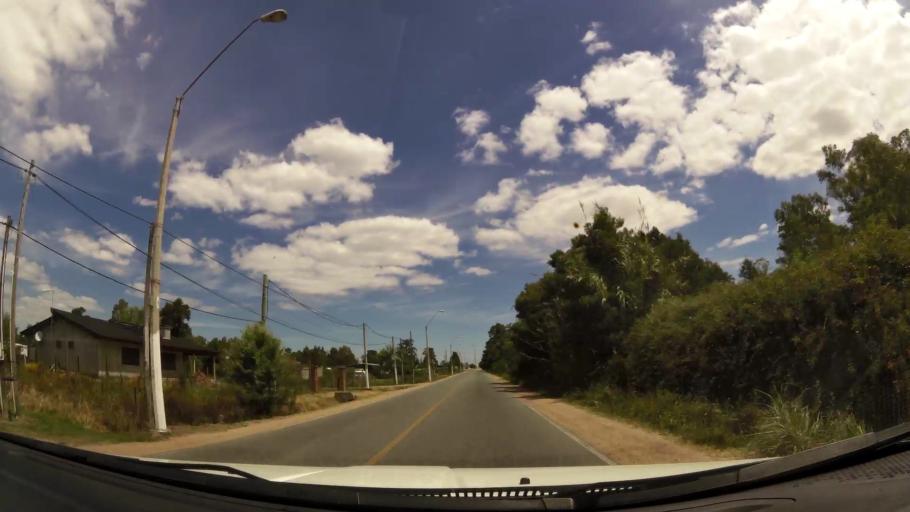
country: UY
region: San Jose
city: Delta del Tigre
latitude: -34.7365
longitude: -56.4473
